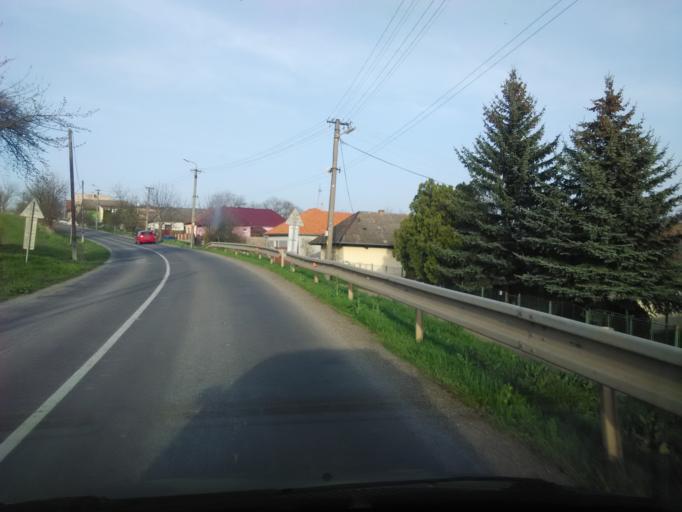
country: SK
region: Nitriansky
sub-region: Okres Nitra
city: Vrable
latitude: 48.1460
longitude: 18.4092
